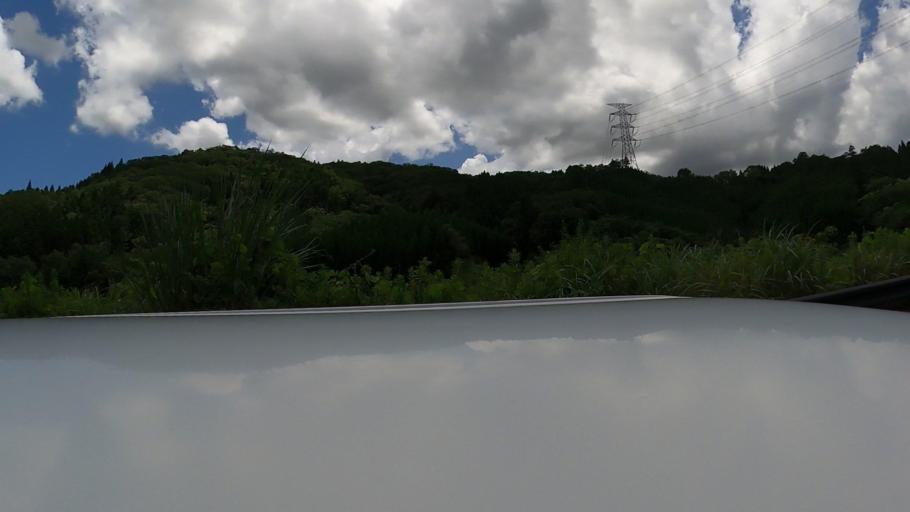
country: JP
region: Miyazaki
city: Nobeoka
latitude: 32.5788
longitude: 131.5213
